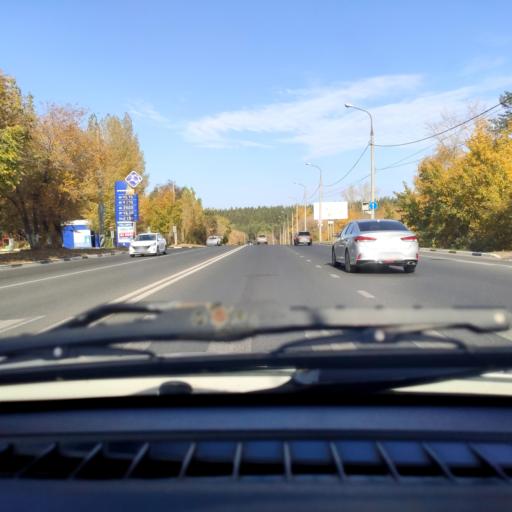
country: RU
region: Samara
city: Zhigulevsk
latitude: 53.4986
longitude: 49.4729
